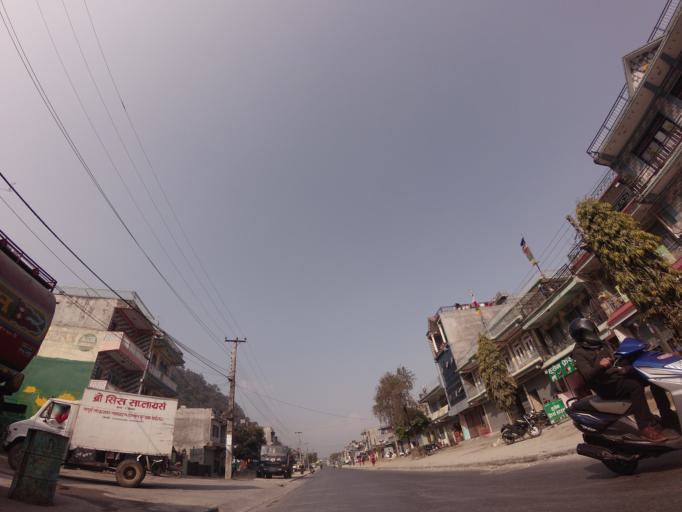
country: NP
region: Western Region
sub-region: Gandaki Zone
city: Pokhara
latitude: 28.2453
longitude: 83.9809
